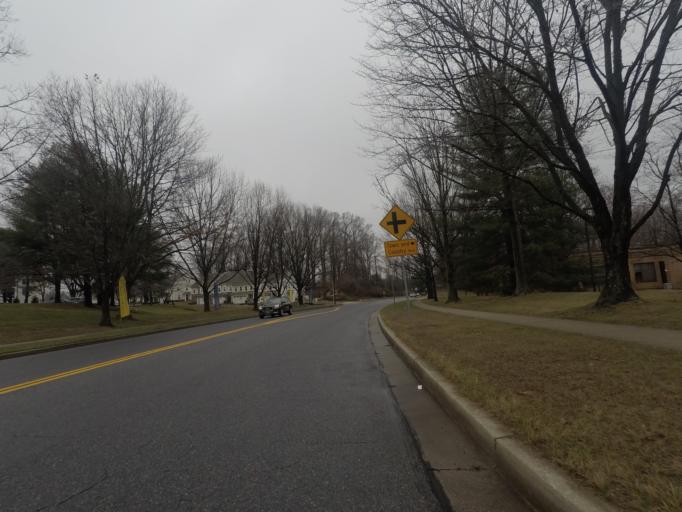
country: US
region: Maryland
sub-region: Howard County
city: Ellicott City
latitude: 39.2864
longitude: -76.8210
